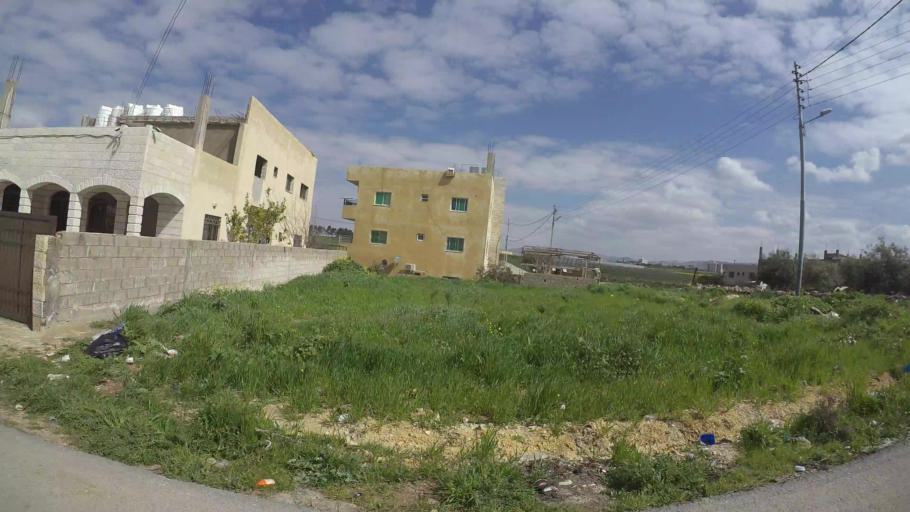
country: JO
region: Amman
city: Al Jubayhah
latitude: 32.0663
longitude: 35.8229
